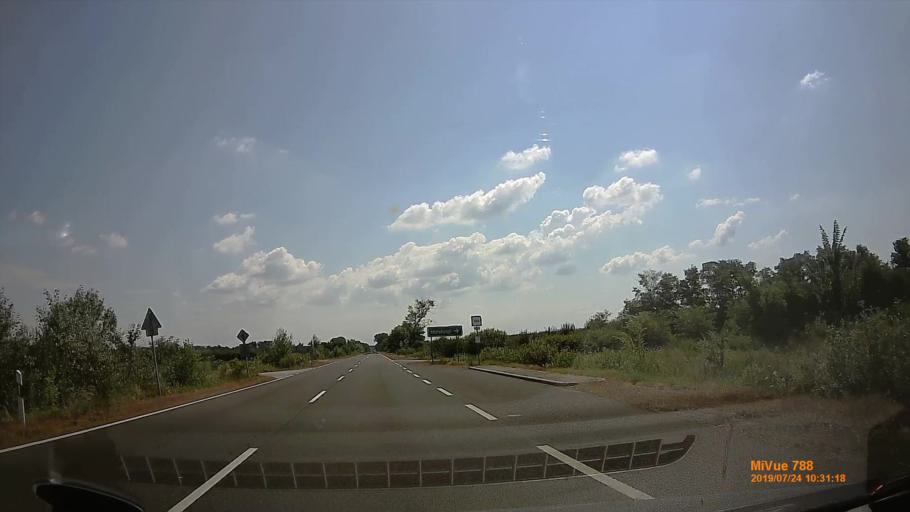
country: HU
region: Szabolcs-Szatmar-Bereg
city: Tarpa
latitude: 48.1603
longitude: 22.5094
